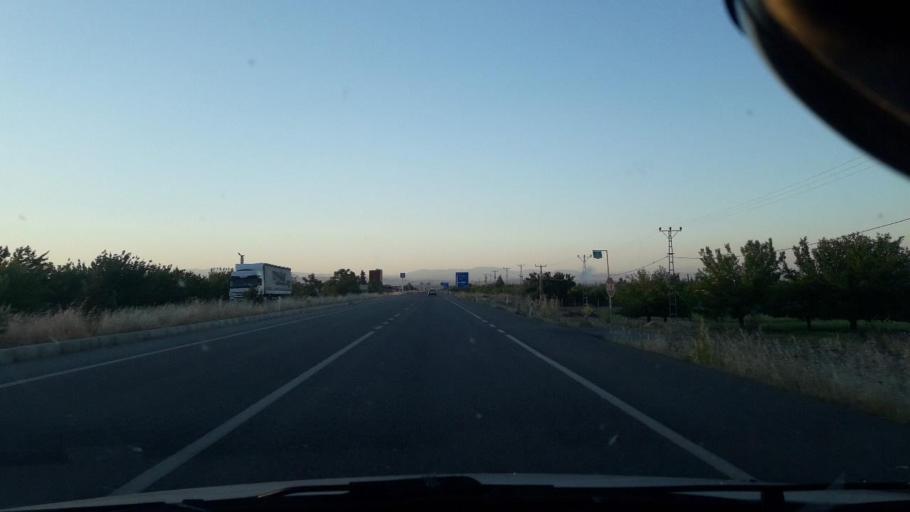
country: TR
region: Malatya
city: Malatya
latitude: 38.4419
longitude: 38.2260
